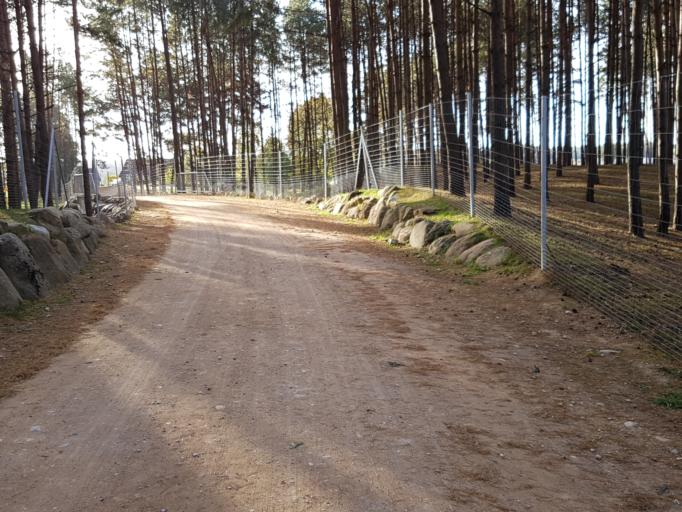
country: LT
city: Moletai
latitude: 55.0393
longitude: 25.4157
